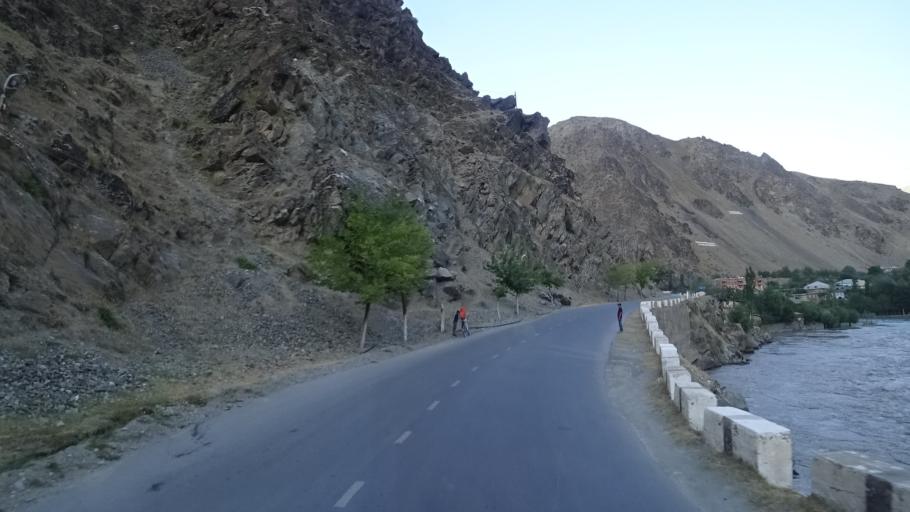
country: TJ
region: Gorno-Badakhshan
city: Qalaikhumb
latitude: 38.4566
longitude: 70.7840
